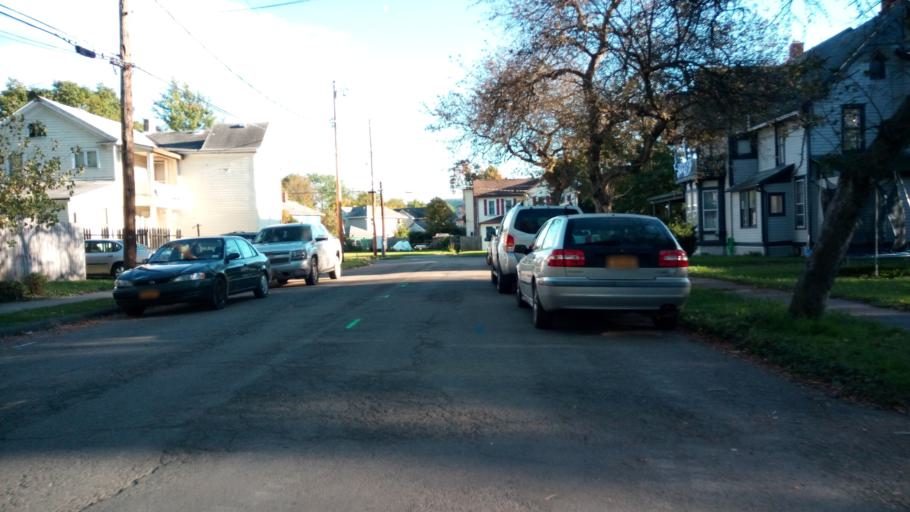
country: US
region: New York
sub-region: Chemung County
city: Elmira
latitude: 42.0753
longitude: -76.8057
